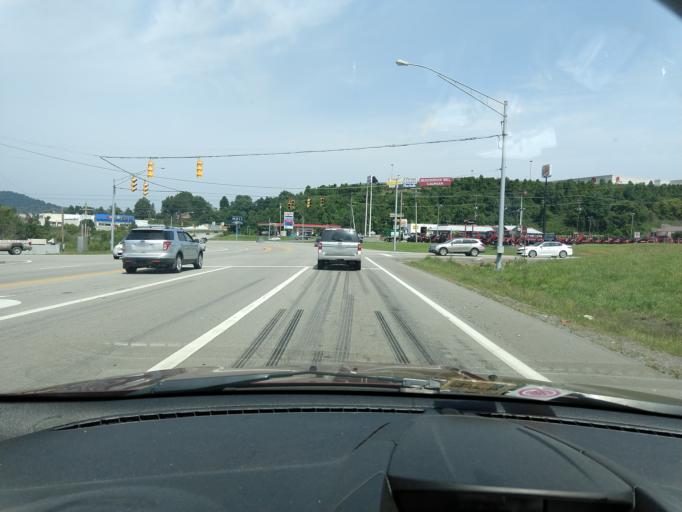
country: US
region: West Virginia
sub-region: Harrison County
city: Bridgeport
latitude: 39.3075
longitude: -80.2748
